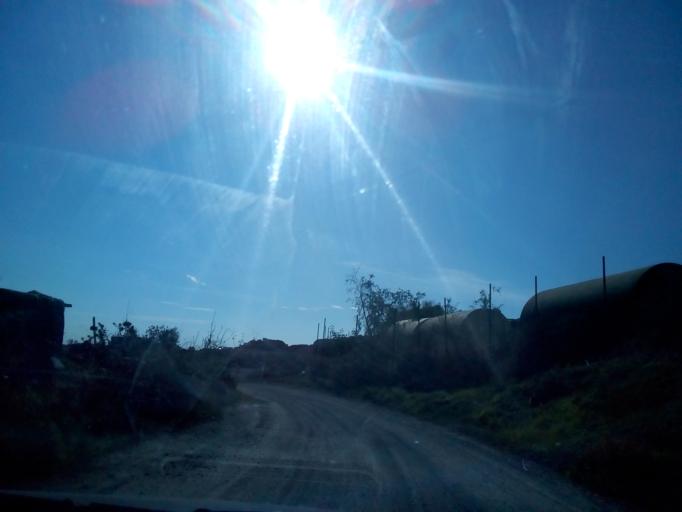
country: CY
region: Limassol
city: Ypsonas
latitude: 34.6774
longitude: 32.9791
